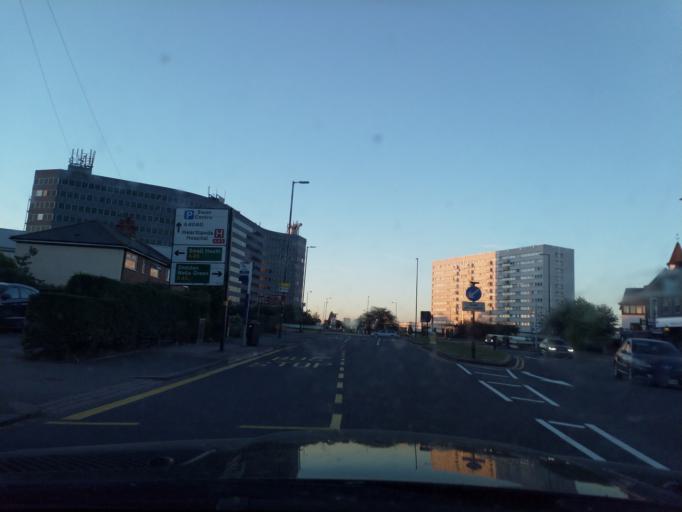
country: GB
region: England
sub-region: City and Borough of Birmingham
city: Acocks Green
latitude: 52.4609
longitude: -1.8167
